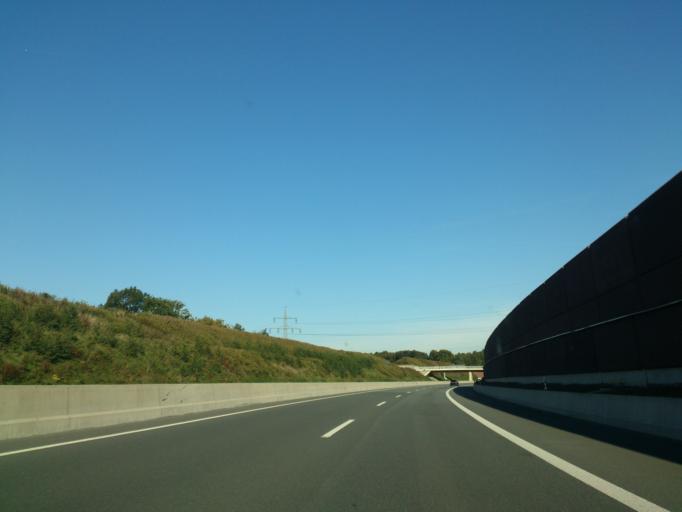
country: DE
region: North Rhine-Westphalia
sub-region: Regierungsbezirk Detmold
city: Verl
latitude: 51.9481
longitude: 8.5091
